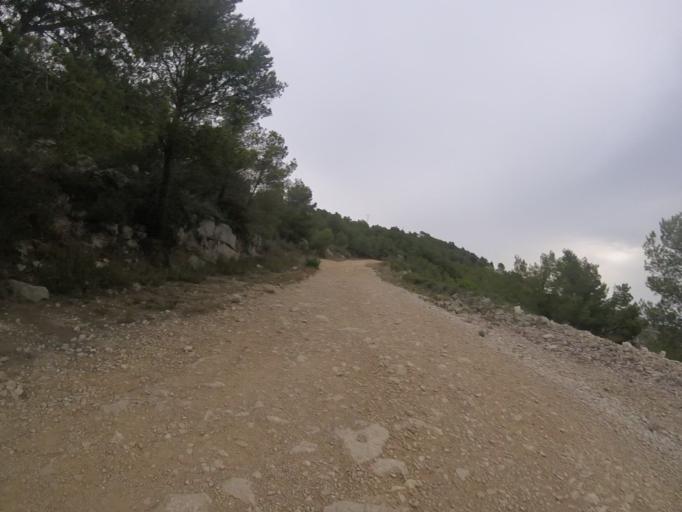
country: ES
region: Valencia
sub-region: Provincia de Castello
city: Alcoceber
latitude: 40.2755
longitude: 0.2804
